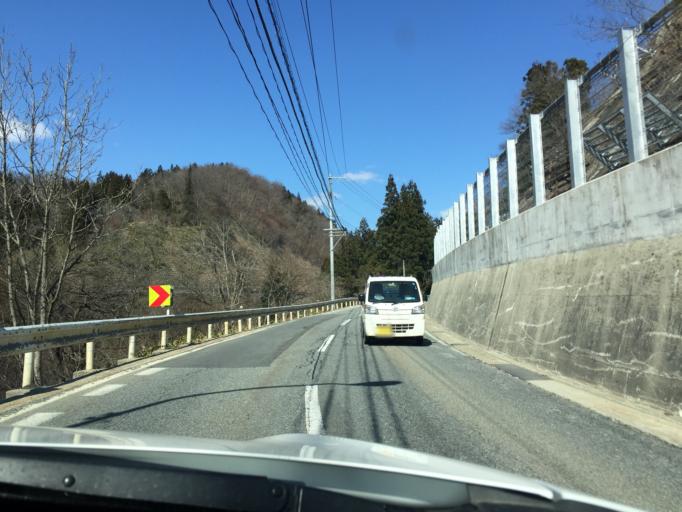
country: JP
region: Yamagata
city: Nagai
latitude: 38.2458
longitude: 140.0960
